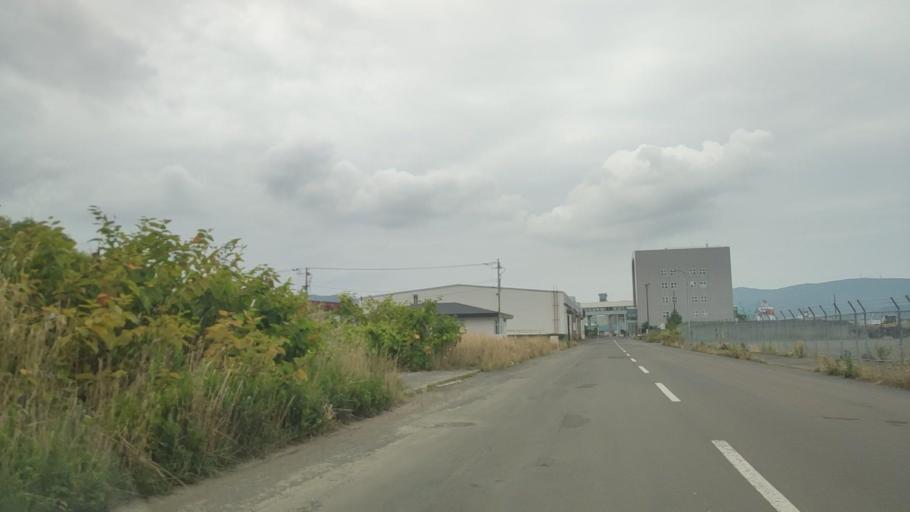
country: JP
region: Hokkaido
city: Otaru
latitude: 43.1892
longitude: 141.0209
